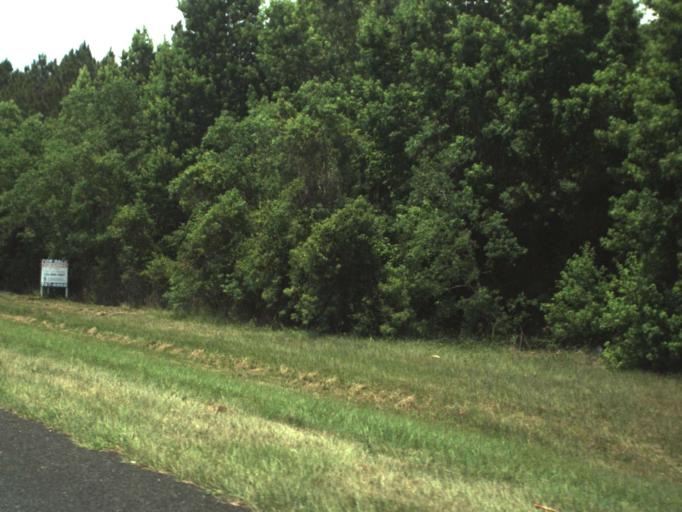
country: US
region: Florida
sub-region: Lake County
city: Fruitland Park
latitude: 28.8163
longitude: -81.9391
